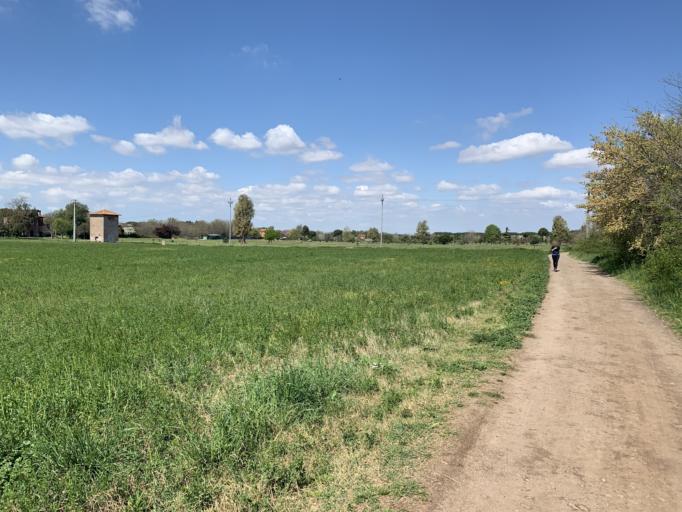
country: IT
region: Latium
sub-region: Citta metropolitana di Roma Capitale
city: Ciampino
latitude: 41.8387
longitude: 12.5685
